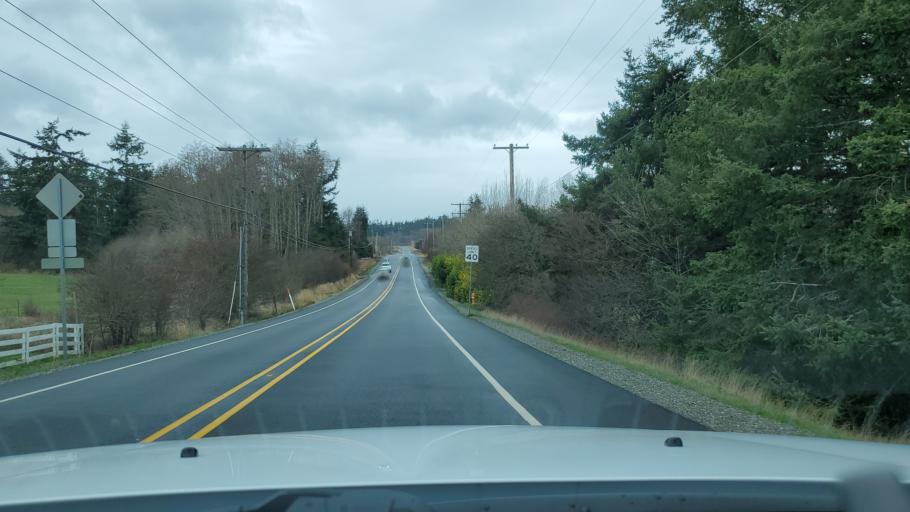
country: US
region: Washington
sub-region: Island County
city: Ault Field
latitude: 48.3259
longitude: -122.6758
